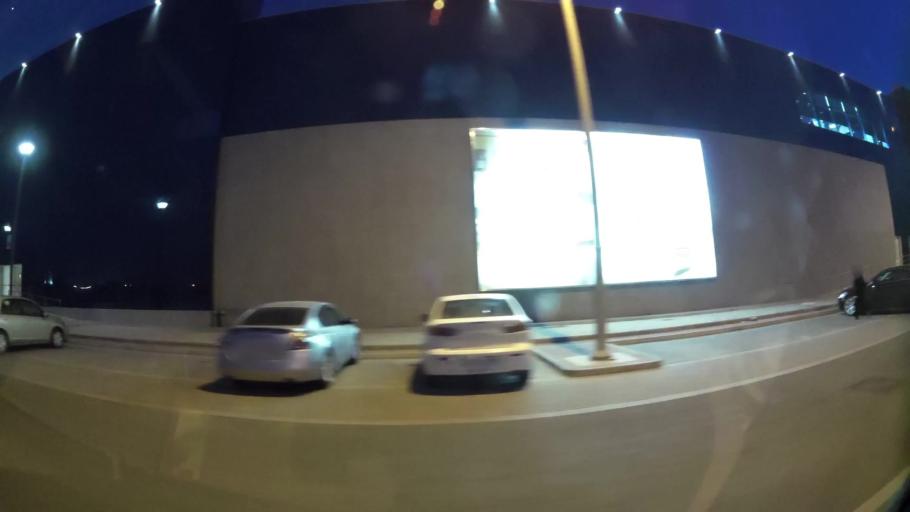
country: QA
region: Baladiyat ad Dawhah
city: Doha
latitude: 25.2560
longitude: 51.4817
